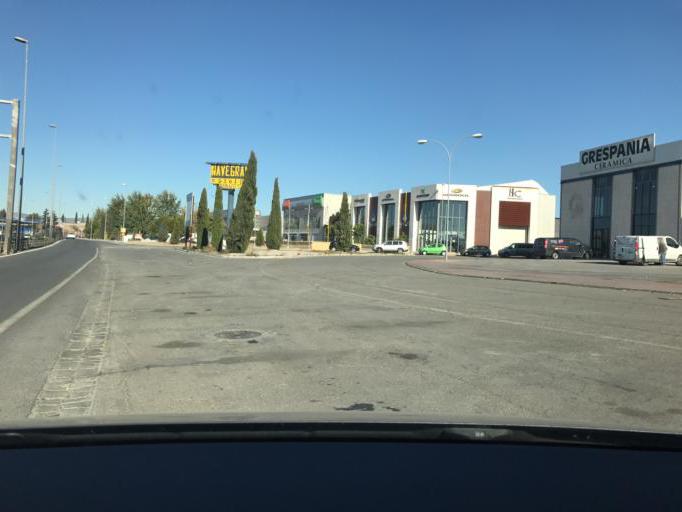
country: ES
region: Andalusia
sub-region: Provincia de Granada
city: Peligros
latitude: 37.2265
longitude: -3.6353
